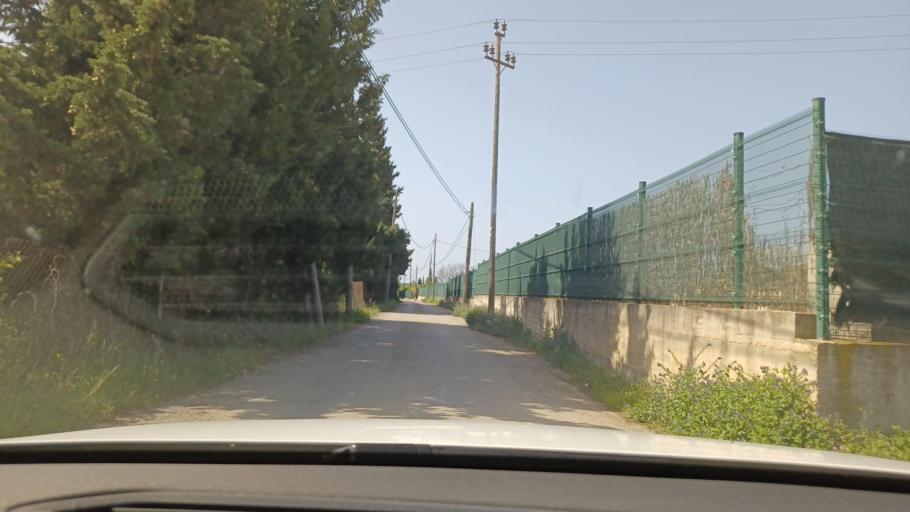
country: ES
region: Catalonia
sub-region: Provincia de Tarragona
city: Tortosa
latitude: 40.7966
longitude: 0.5166
